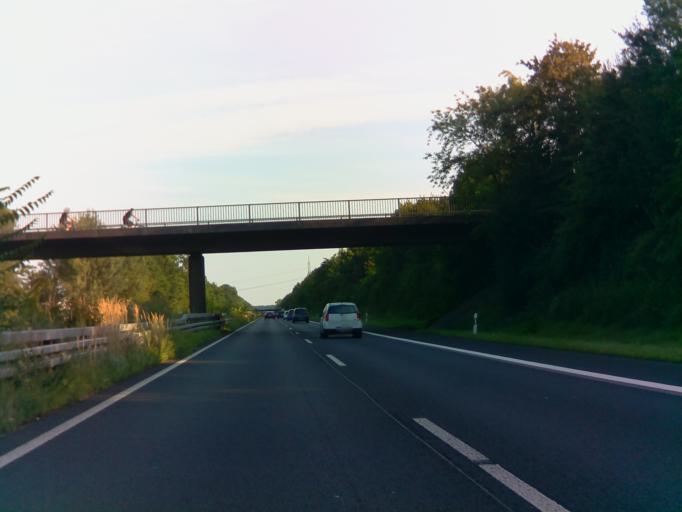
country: DE
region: Hesse
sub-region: Regierungsbezirk Darmstadt
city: Rodgau
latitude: 50.0297
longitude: 8.8918
